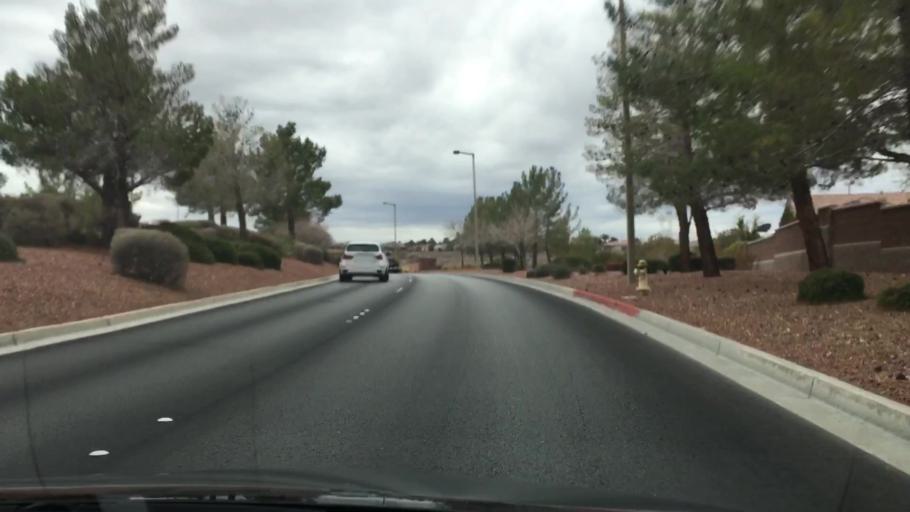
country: US
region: Nevada
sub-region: Clark County
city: Whitney
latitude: 35.9651
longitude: -115.0982
